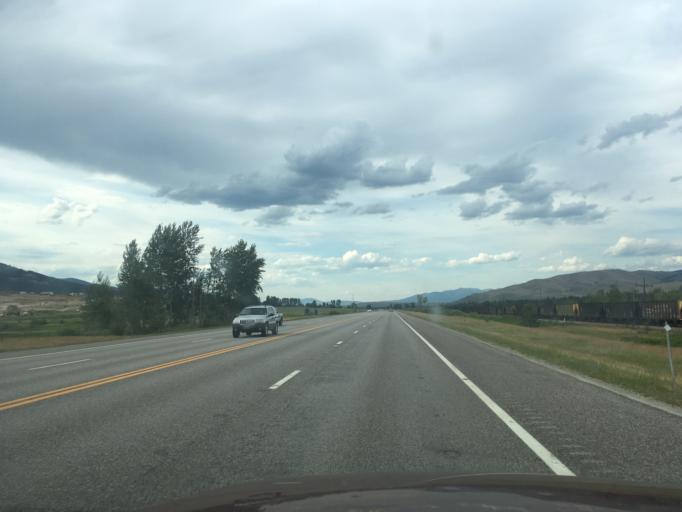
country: US
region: Montana
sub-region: Missoula County
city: Lolo
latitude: 46.6866
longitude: -114.0742
